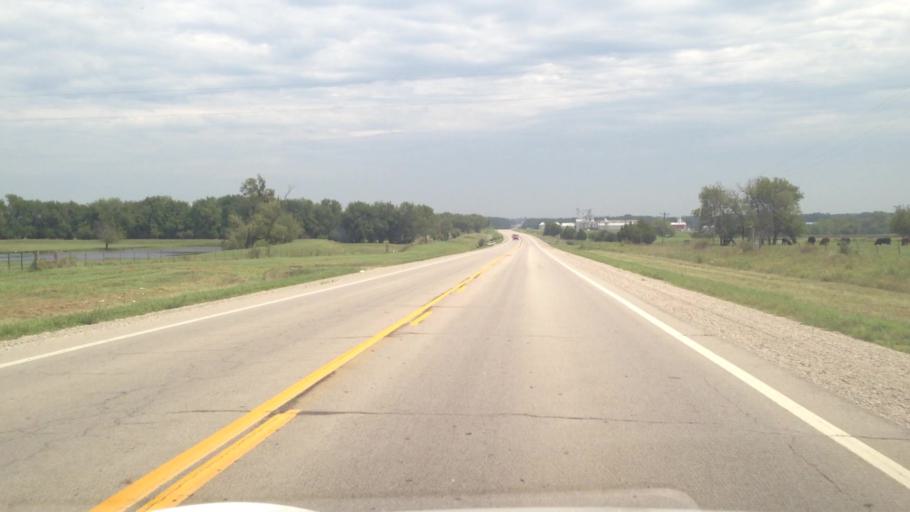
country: US
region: Kansas
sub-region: Crawford County
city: Girard
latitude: 37.5144
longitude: -94.9233
